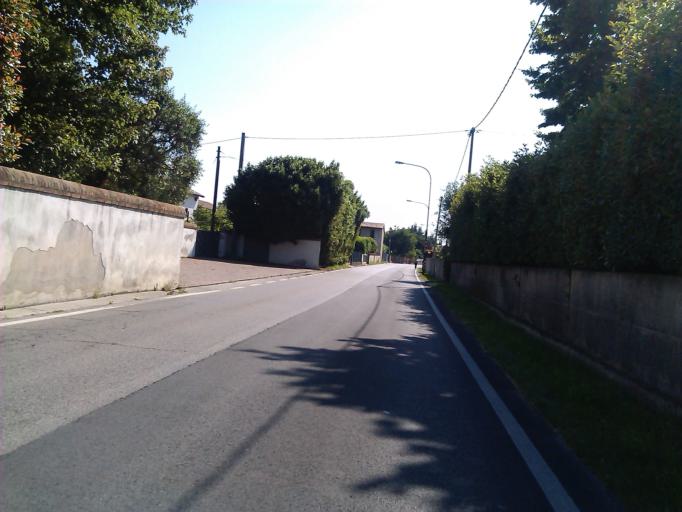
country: IT
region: Veneto
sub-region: Provincia di Vicenza
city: San Zeno-San Giuseppe
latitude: 45.7567
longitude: 11.7707
